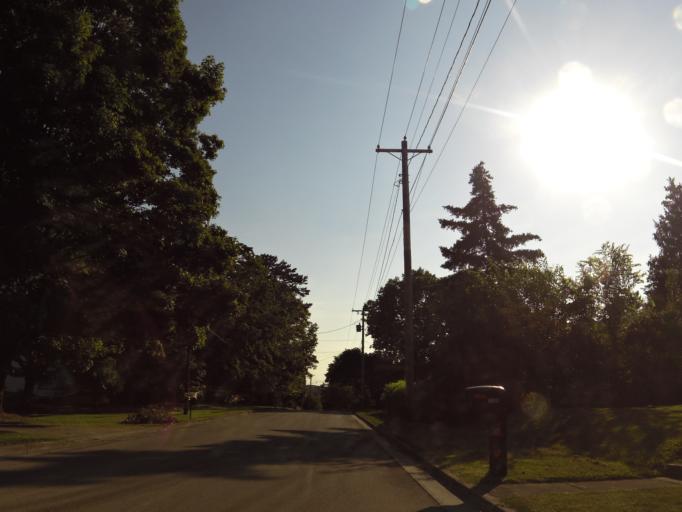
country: US
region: Tennessee
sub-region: Blount County
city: Maryville
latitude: 35.7626
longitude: -83.9610
